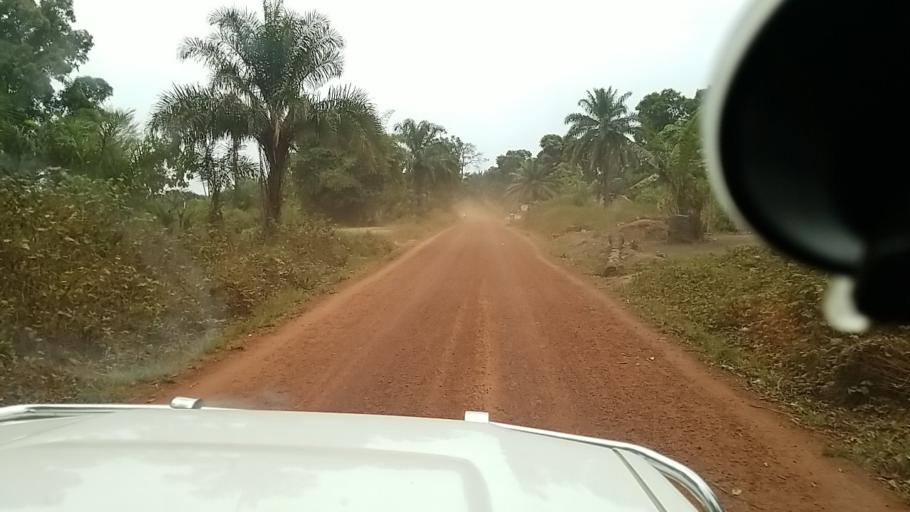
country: CD
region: Equateur
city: Libenge
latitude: 3.7265
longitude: 18.7715
